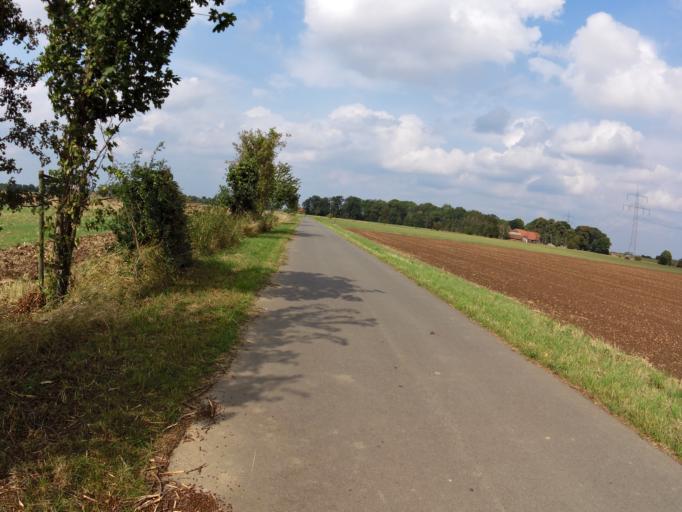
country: DE
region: Lower Saxony
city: Hilgermissen
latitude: 52.8799
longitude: 9.1761
